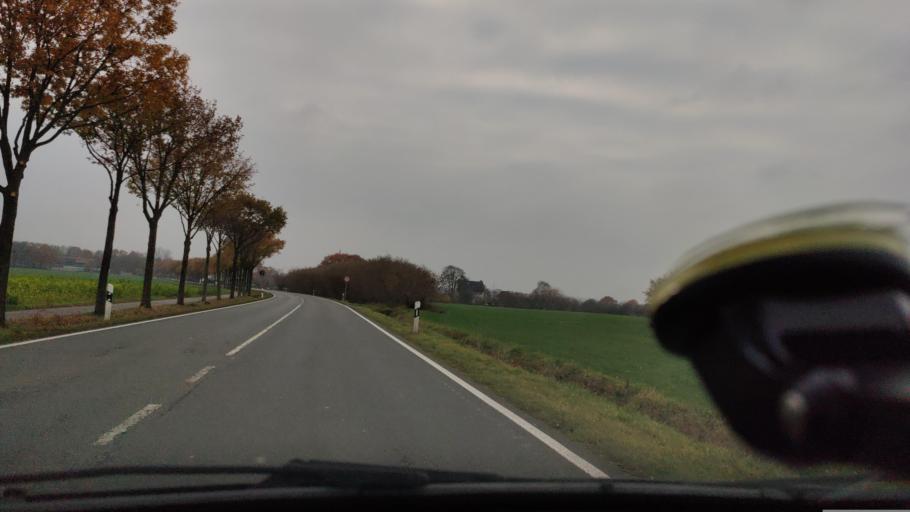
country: DE
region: North Rhine-Westphalia
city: Lunen
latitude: 51.6387
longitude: 7.5090
